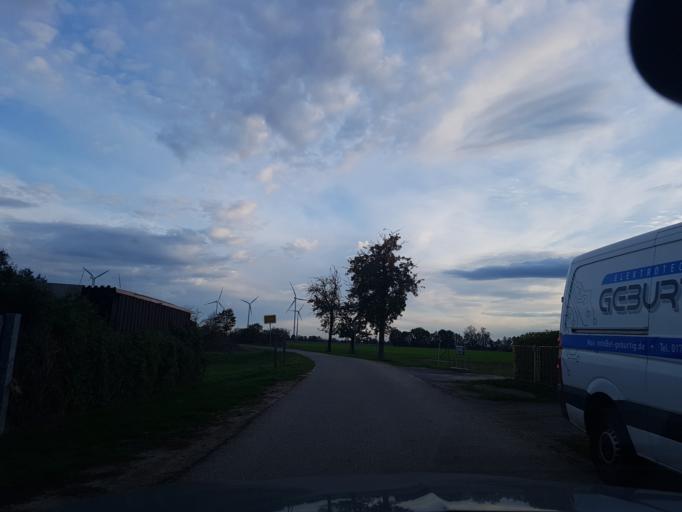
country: DE
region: Brandenburg
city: Elsterwerda
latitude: 51.4578
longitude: 13.4681
